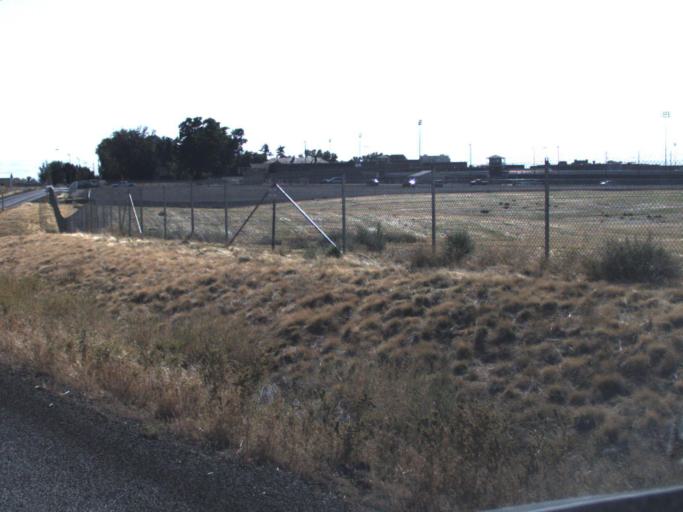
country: US
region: Washington
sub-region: Walla Walla County
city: Walla Walla
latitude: 46.0846
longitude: -118.3566
